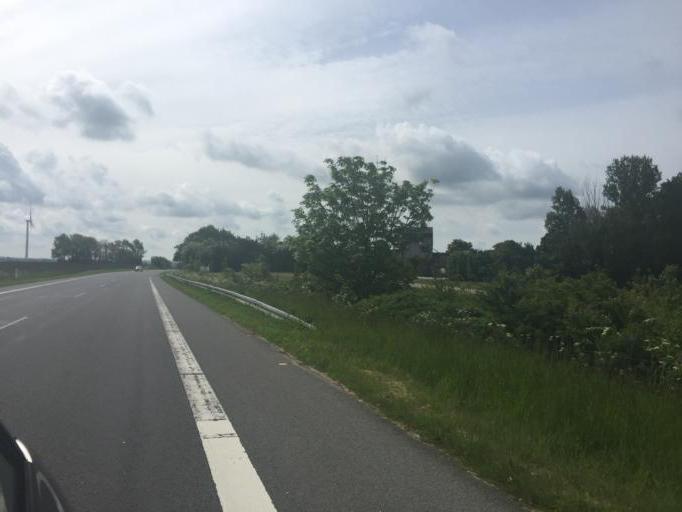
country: DK
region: Zealand
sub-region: Kalundborg Kommune
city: Hong
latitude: 55.5126
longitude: 11.3810
